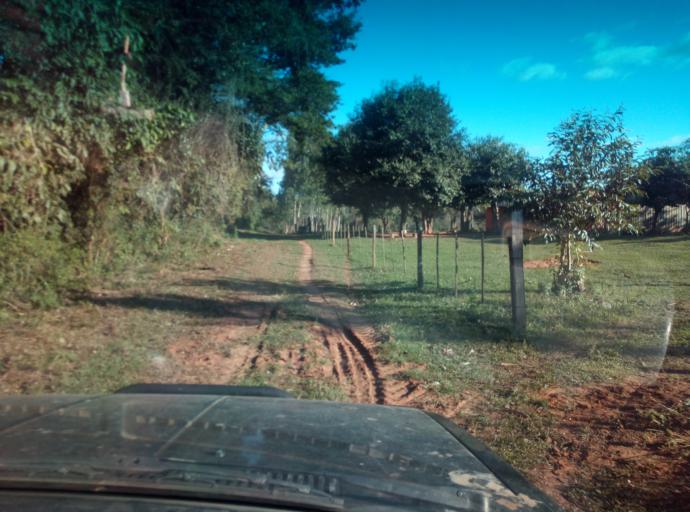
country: PY
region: Caaguazu
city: Carayao
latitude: -25.1881
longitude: -56.2627
